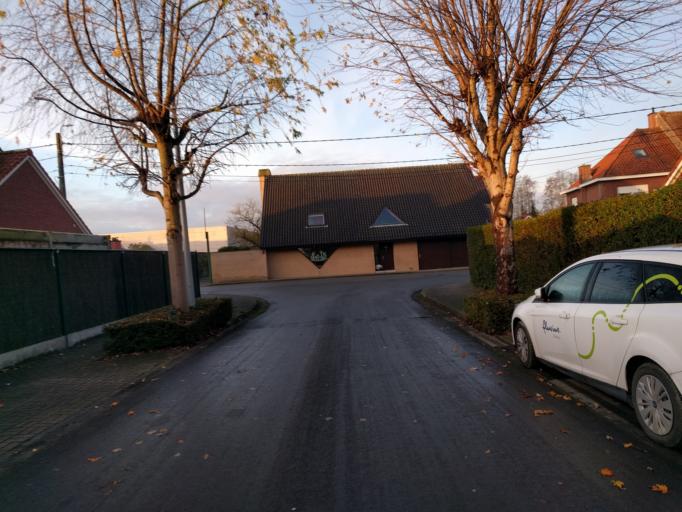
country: BE
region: Flanders
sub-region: Provincie West-Vlaanderen
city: Wevelgem
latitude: 50.8056
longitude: 3.1667
